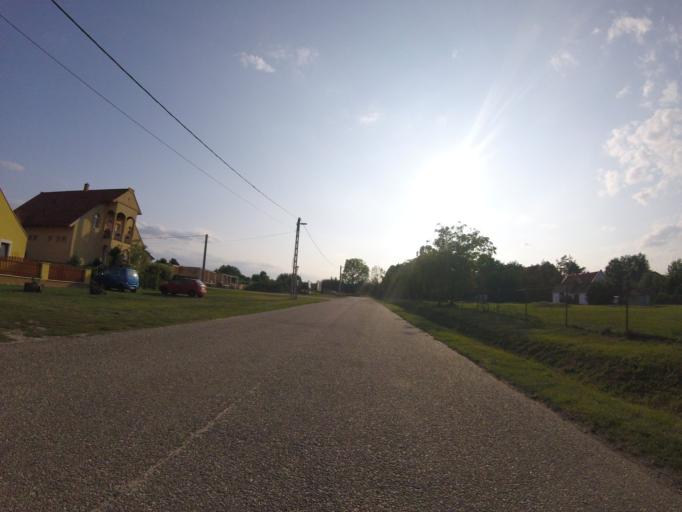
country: HU
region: Gyor-Moson-Sopron
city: Fertod
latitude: 47.6195
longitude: 16.7873
